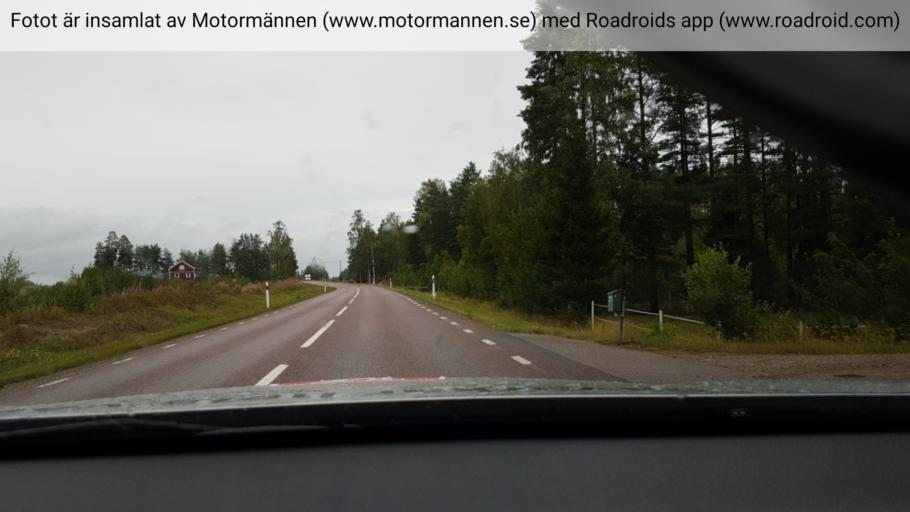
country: SE
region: Gaevleborg
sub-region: Gavle Kommun
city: Valbo
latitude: 60.5831
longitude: 16.9673
